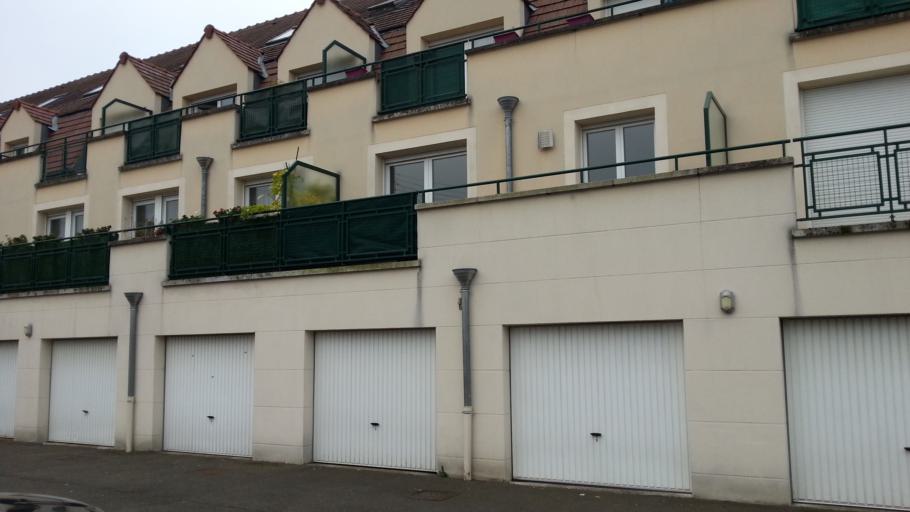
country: FR
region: Picardie
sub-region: Departement de l'Oise
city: Chambly
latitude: 49.1672
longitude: 2.2471
